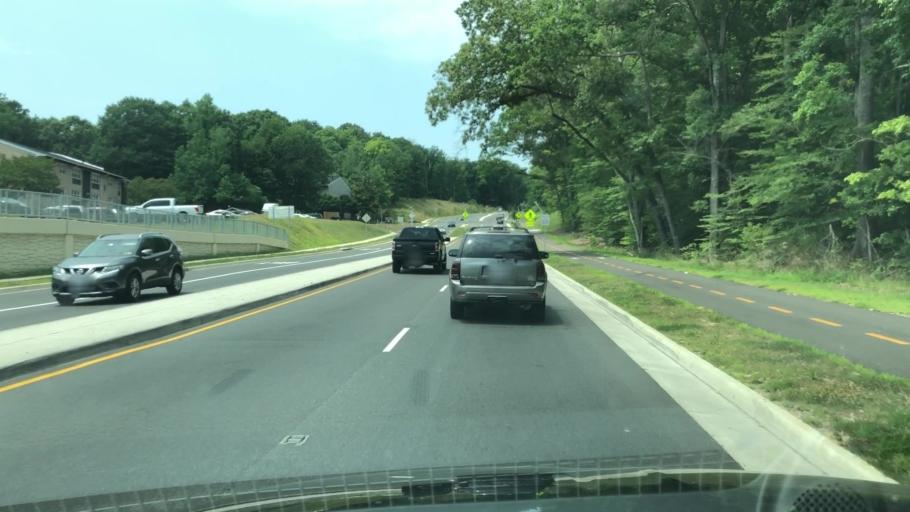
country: US
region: Virginia
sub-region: Stafford County
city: Falmouth
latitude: 38.3165
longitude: -77.4874
